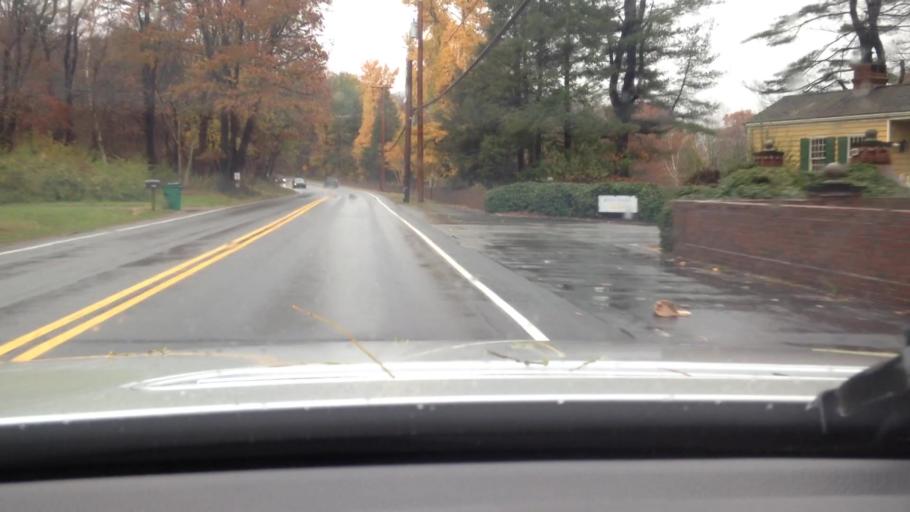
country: US
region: New York
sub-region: Putnam County
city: Cold Spring
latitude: 41.4140
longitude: -73.9382
